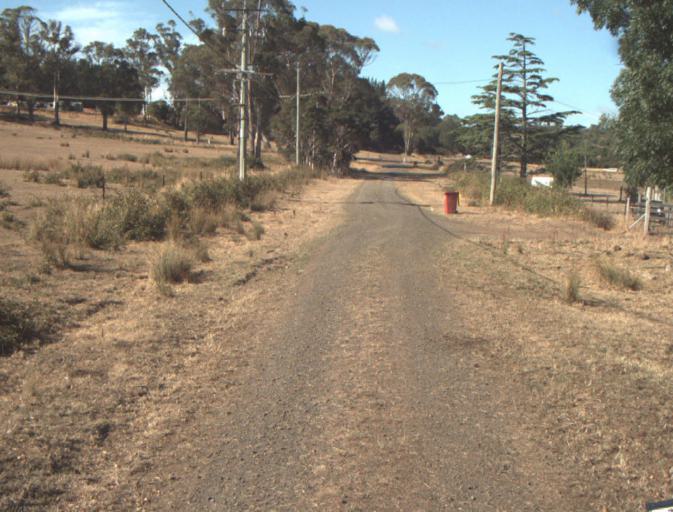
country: AU
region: Tasmania
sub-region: Dorset
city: Bridport
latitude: -41.1426
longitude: 147.2125
